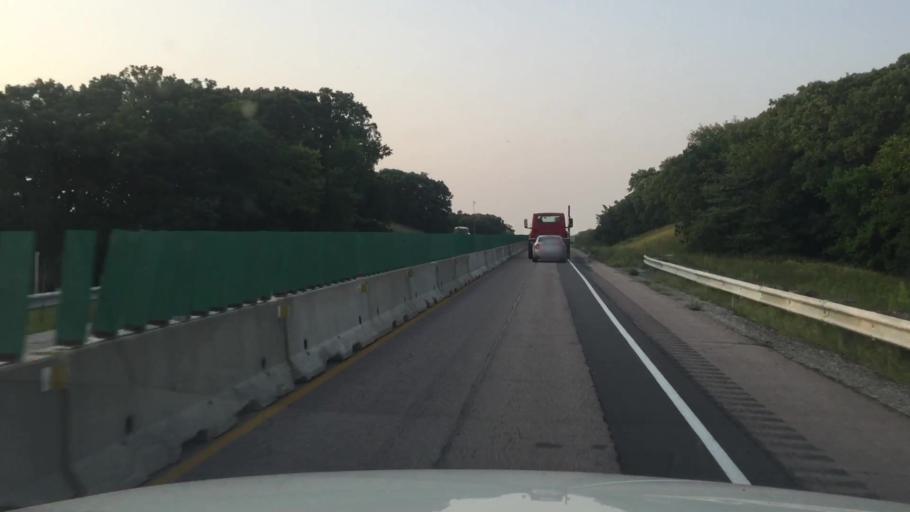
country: US
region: Iowa
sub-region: Decatur County
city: Leon
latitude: 40.7034
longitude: -93.8458
